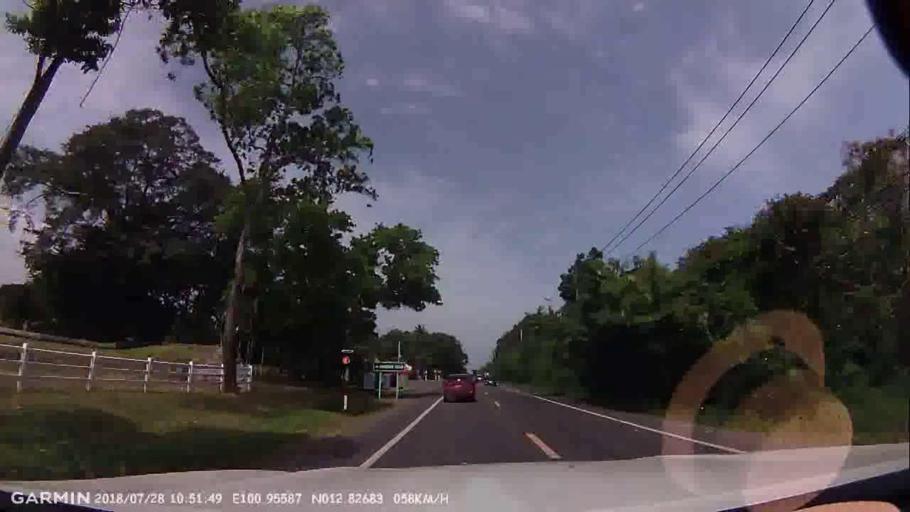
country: TH
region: Chon Buri
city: Phatthaya
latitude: 12.8268
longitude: 100.9557
